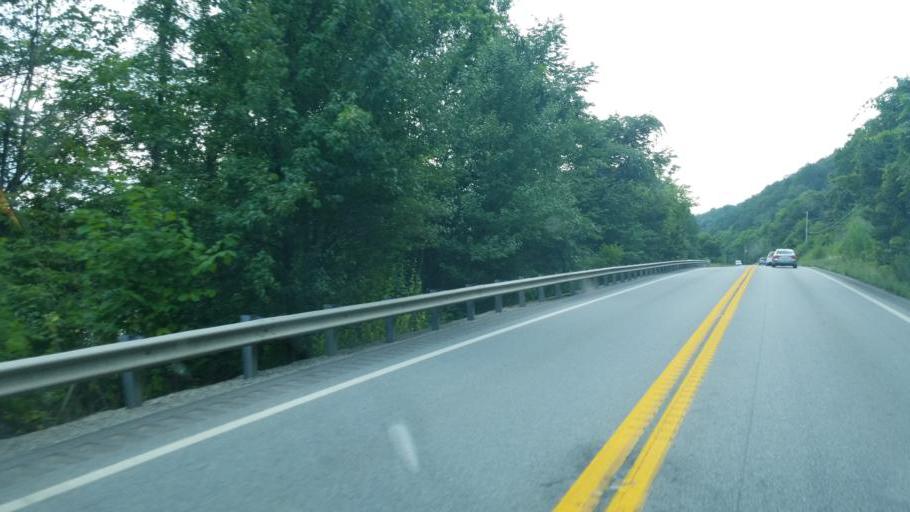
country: US
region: West Virginia
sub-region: Putnam County
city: Buffalo
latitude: 38.6053
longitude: -82.0015
